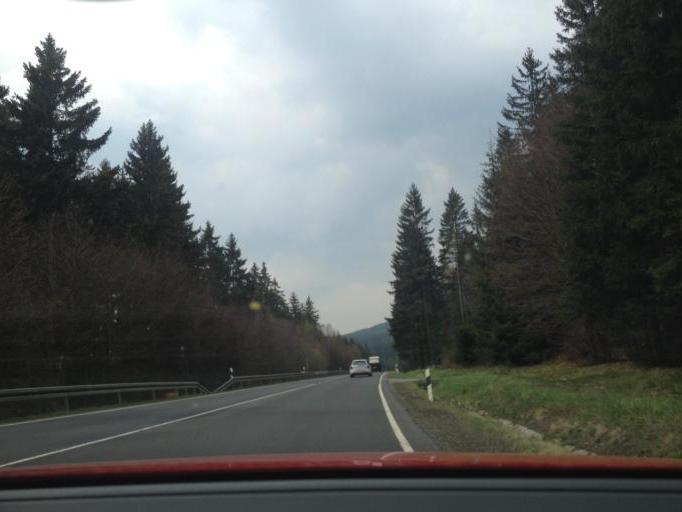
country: DE
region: Bavaria
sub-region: Upper Franconia
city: Fichtelberg
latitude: 50.0127
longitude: 11.8795
